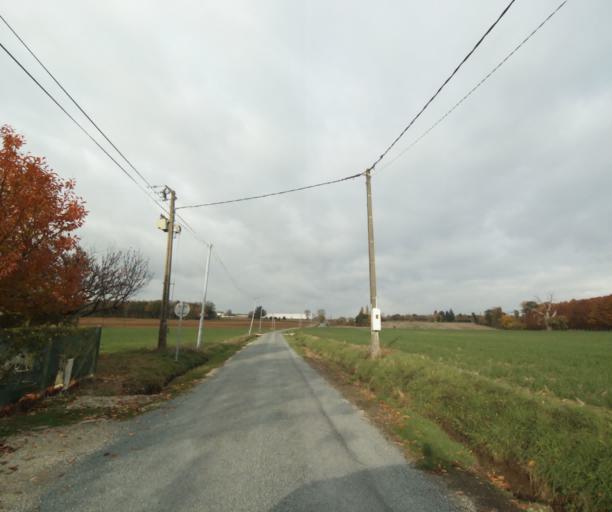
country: FR
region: Poitou-Charentes
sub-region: Departement de la Charente-Maritime
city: Saint-Georges-des-Coteaux
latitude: 45.7876
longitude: -0.7306
